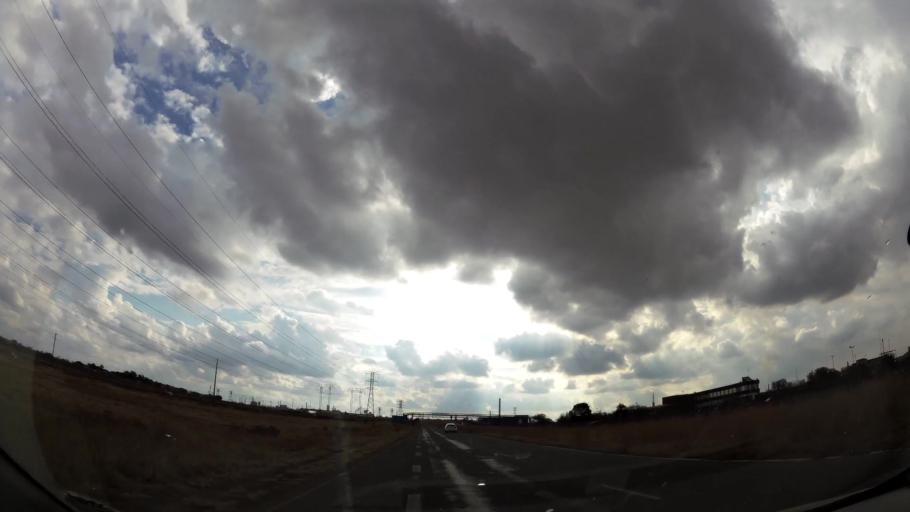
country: ZA
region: Orange Free State
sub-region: Fezile Dabi District Municipality
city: Sasolburg
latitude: -26.8362
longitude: 27.8675
